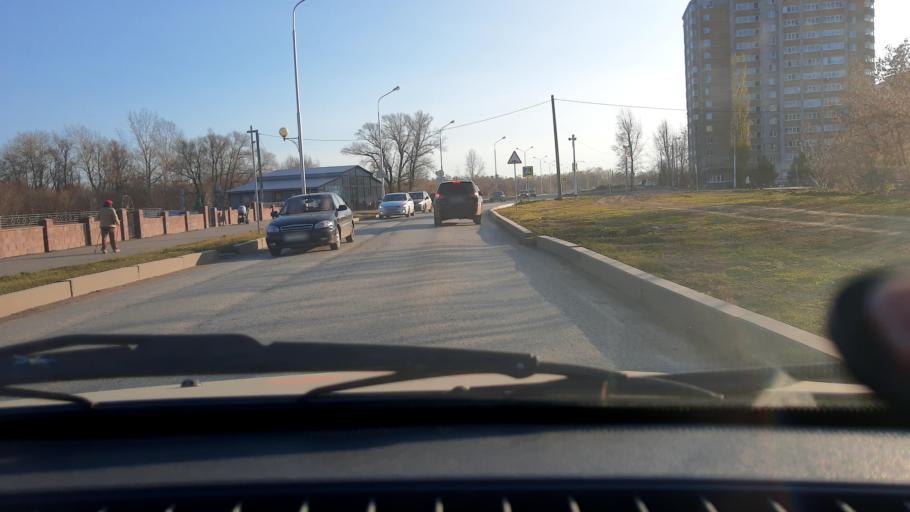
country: RU
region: Bashkortostan
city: Ufa
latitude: 54.7744
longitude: 56.0850
